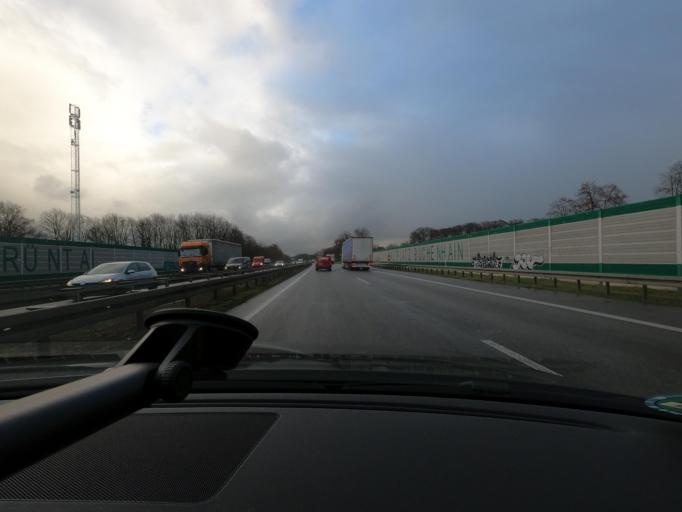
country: DE
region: North Rhine-Westphalia
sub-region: Regierungsbezirk Arnsberg
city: Frondenberg
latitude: 51.5249
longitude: 7.7918
